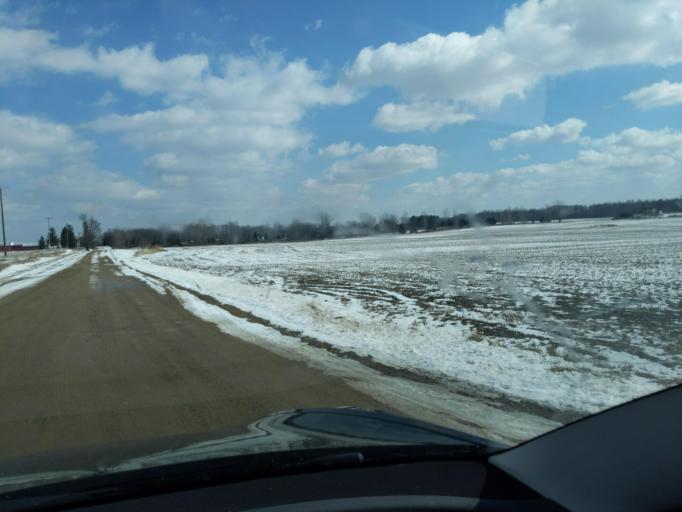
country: US
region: Michigan
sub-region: Livingston County
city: Fowlerville
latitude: 42.6139
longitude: -84.0711
